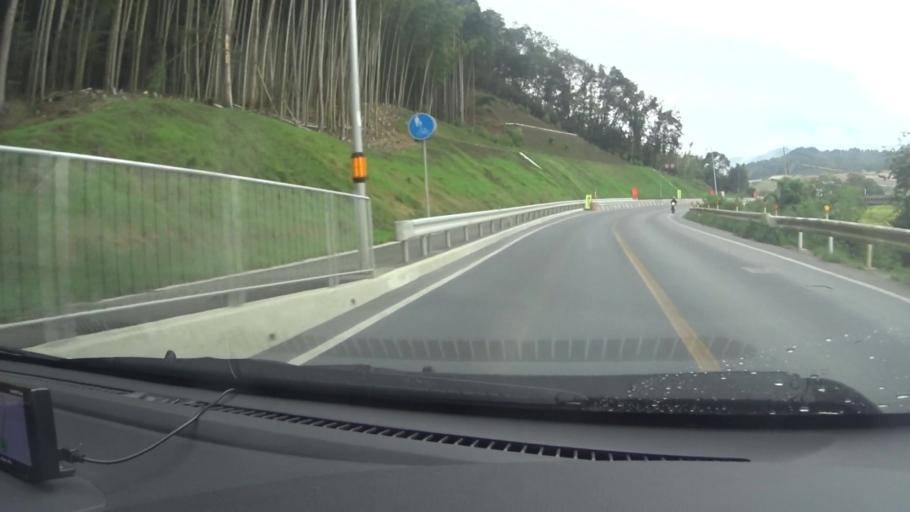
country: JP
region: Kyoto
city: Ayabe
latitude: 35.1882
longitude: 135.3647
